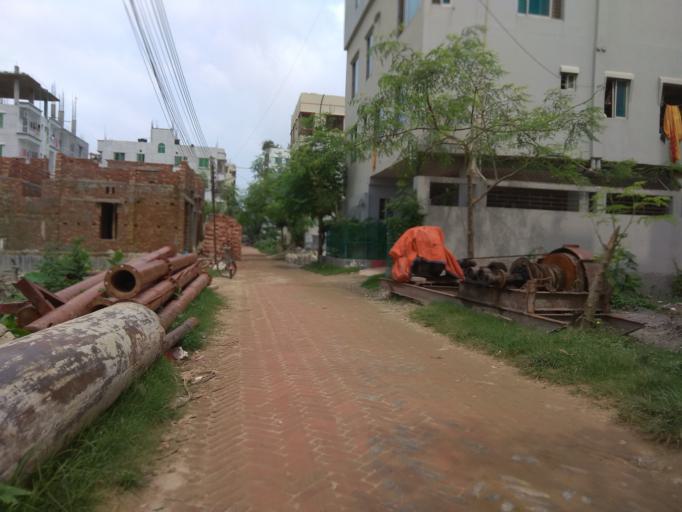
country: BD
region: Dhaka
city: Tungi
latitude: 23.8288
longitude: 90.3491
